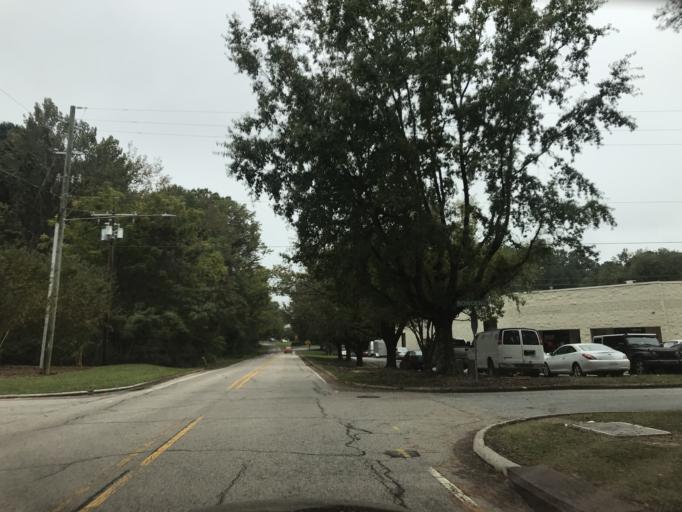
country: US
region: North Carolina
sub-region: Wake County
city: Cary
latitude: 35.7906
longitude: -78.7763
